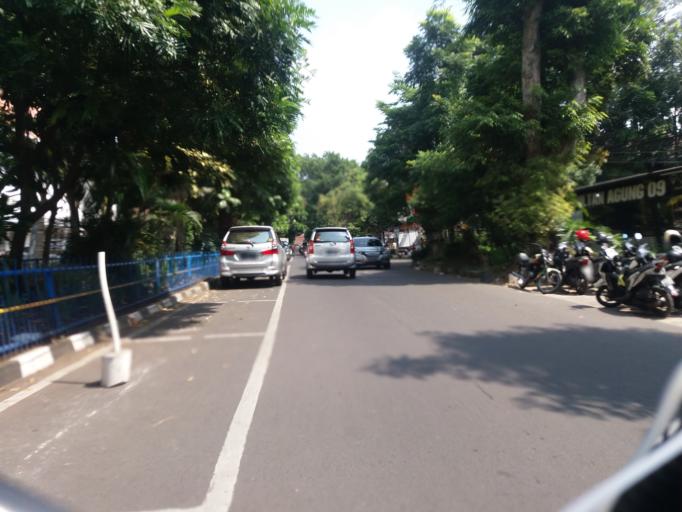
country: ID
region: West Java
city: Bandung
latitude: -6.9045
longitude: 107.6123
